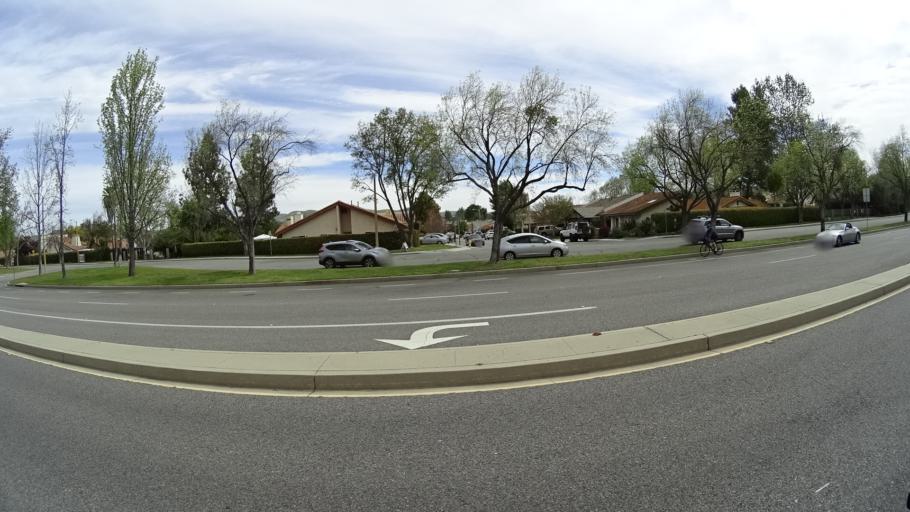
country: US
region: California
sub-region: Los Angeles County
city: Westlake Village
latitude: 34.1415
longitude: -118.8343
